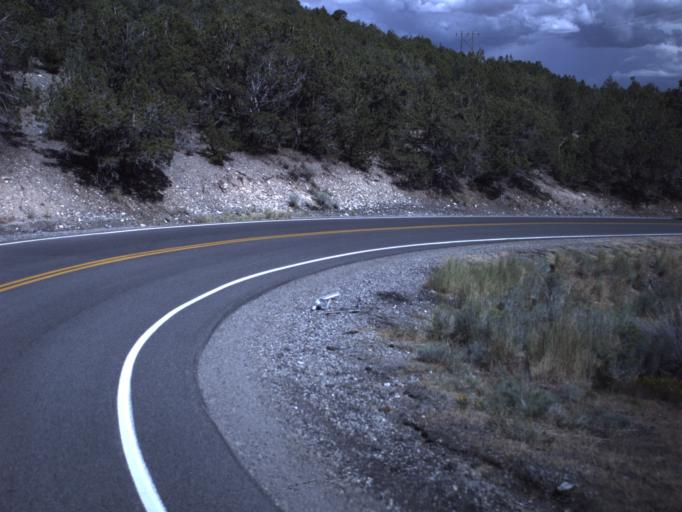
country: US
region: Utah
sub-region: Tooele County
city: Grantsville
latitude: 40.3493
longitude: -112.5580
